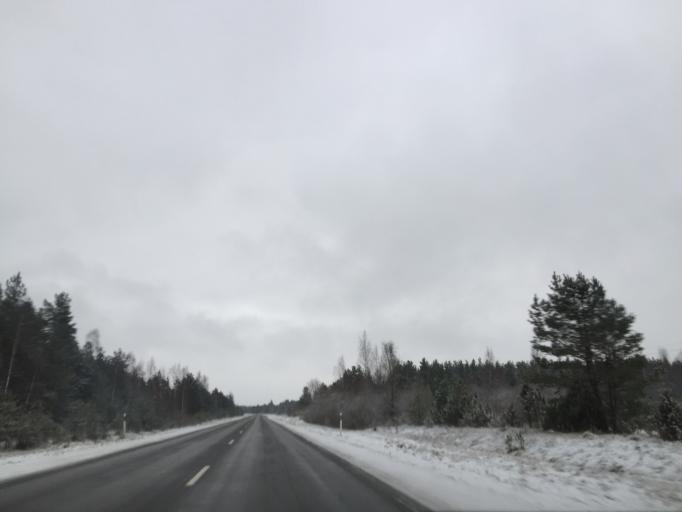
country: EE
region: Laeaene
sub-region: Lihula vald
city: Lihula
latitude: 58.6164
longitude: 23.9137
